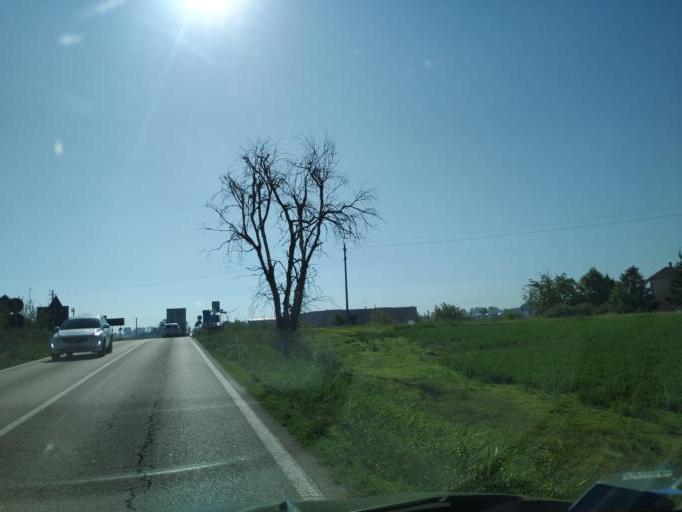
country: IT
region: Emilia-Romagna
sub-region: Provincia di Bologna
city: Sant'Agata Bolognese
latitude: 44.6704
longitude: 11.0917
